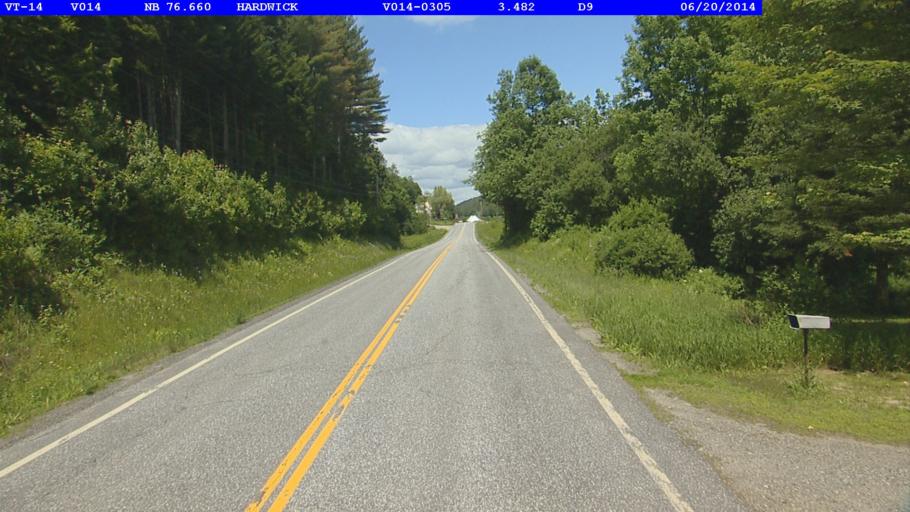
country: US
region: Vermont
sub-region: Caledonia County
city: Hardwick
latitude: 44.5443
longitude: -72.3735
